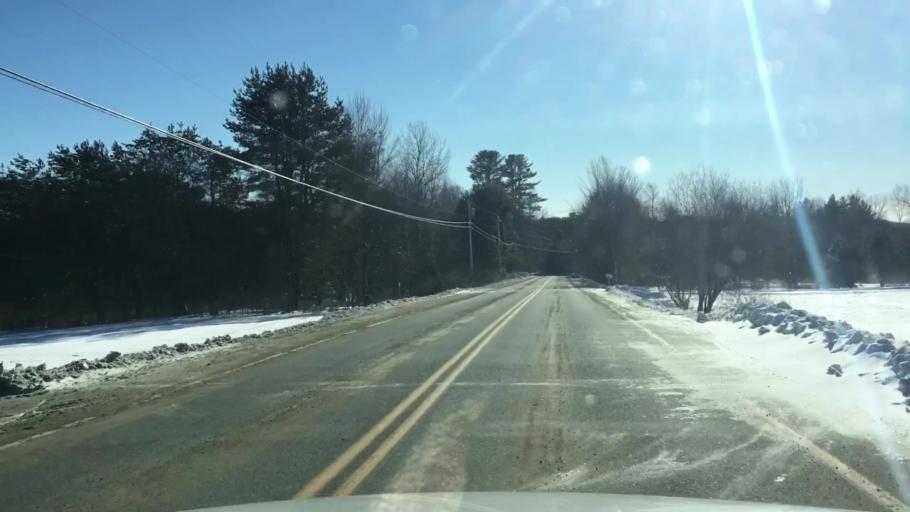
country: US
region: Maine
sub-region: Kennebec County
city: Readfield
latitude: 44.3609
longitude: -69.9904
